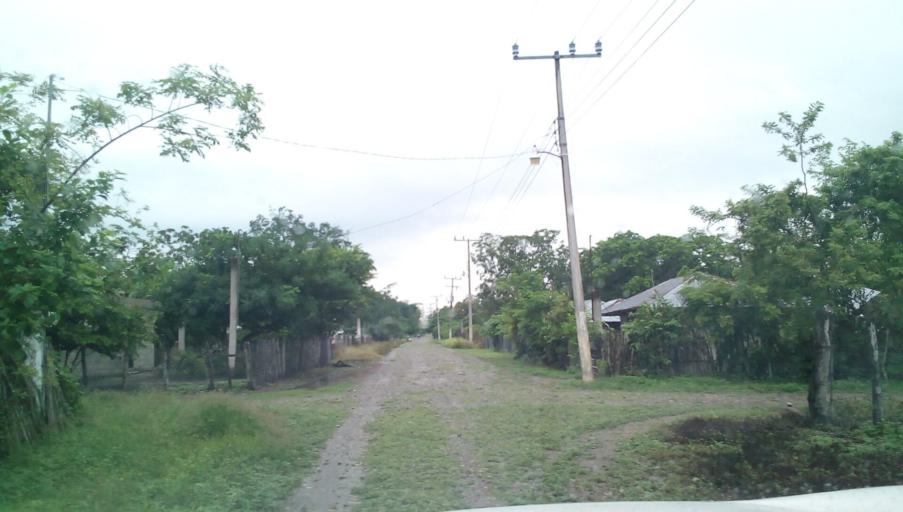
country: MX
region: Veracruz
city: Tempoal de Sanchez
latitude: 21.4167
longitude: -98.4231
